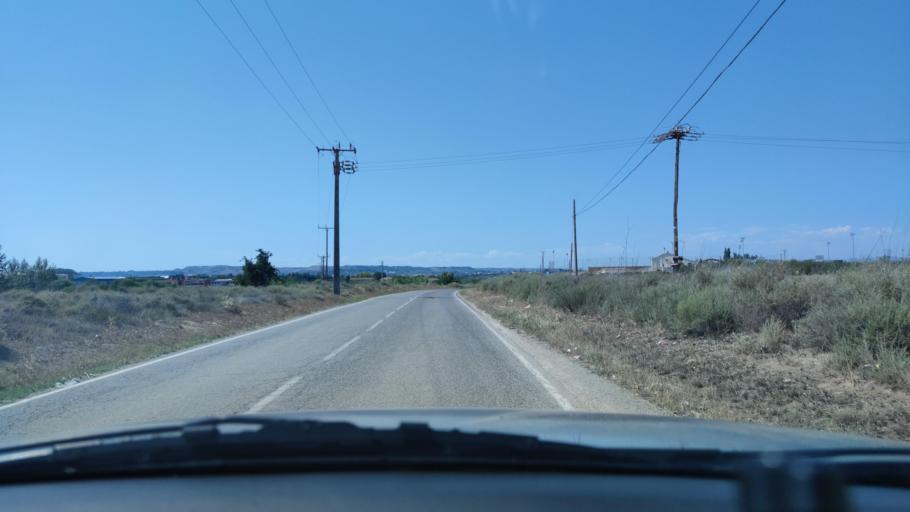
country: ES
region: Catalonia
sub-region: Provincia de Lleida
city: Lleida
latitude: 41.6398
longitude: 0.6256
